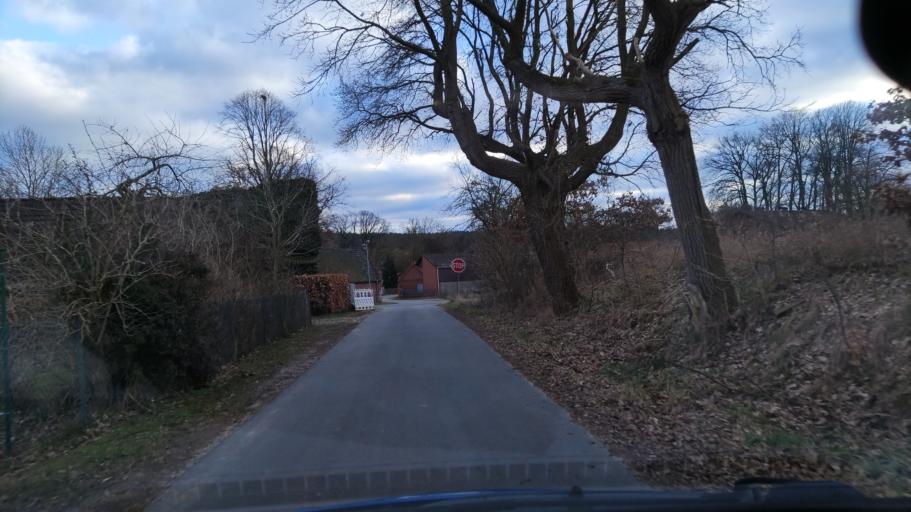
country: DE
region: Lower Saxony
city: Gohrde
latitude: 53.1577
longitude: 10.8550
